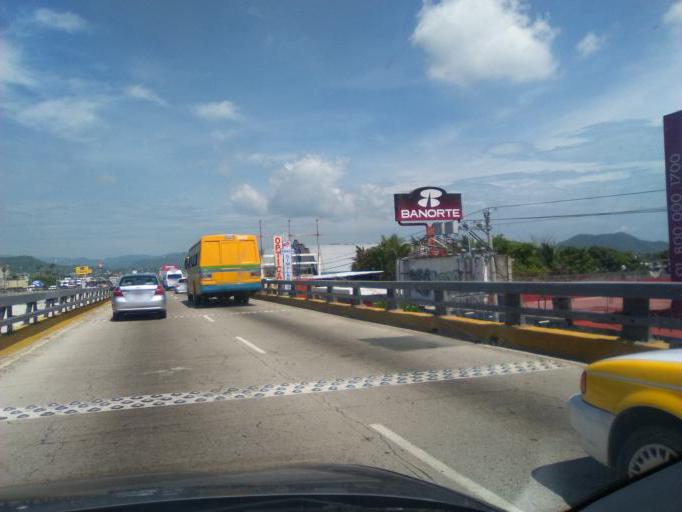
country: MX
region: Guerrero
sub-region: Acapulco de Juarez
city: Nueva Frontera
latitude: 16.8943
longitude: -99.8331
